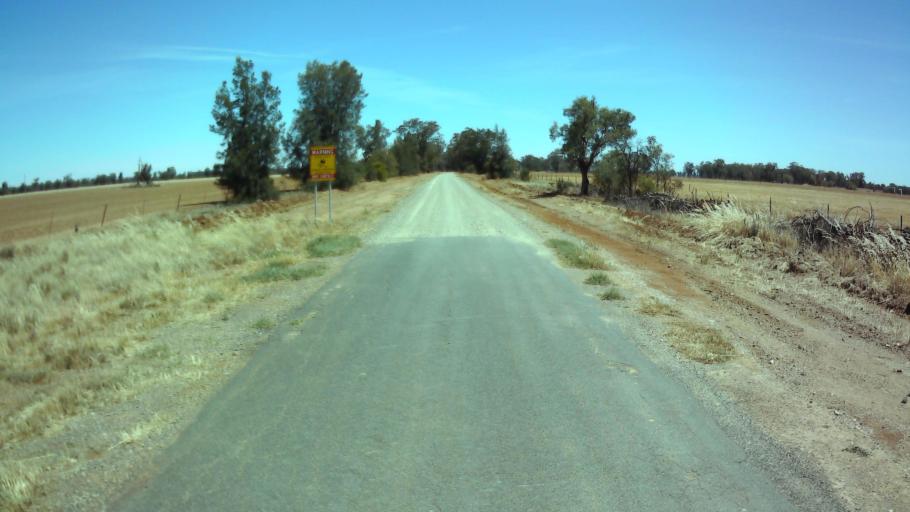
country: AU
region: New South Wales
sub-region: Weddin
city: Grenfell
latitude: -33.9067
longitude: 147.6853
